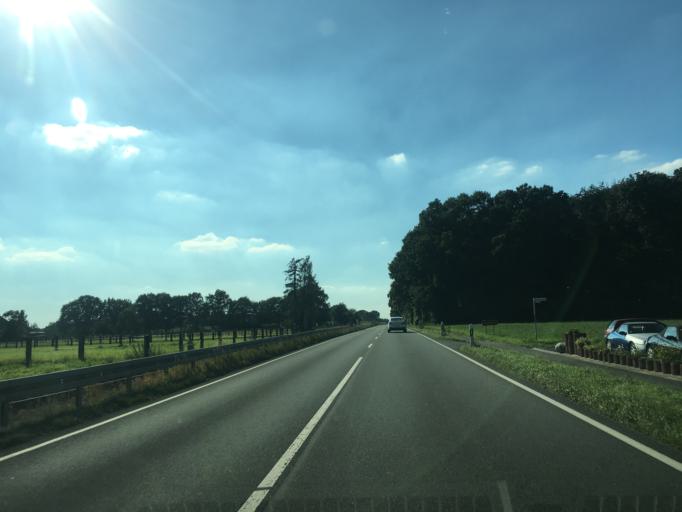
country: DE
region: North Rhine-Westphalia
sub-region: Regierungsbezirk Munster
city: Warendorf
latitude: 51.9552
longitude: 7.9623
